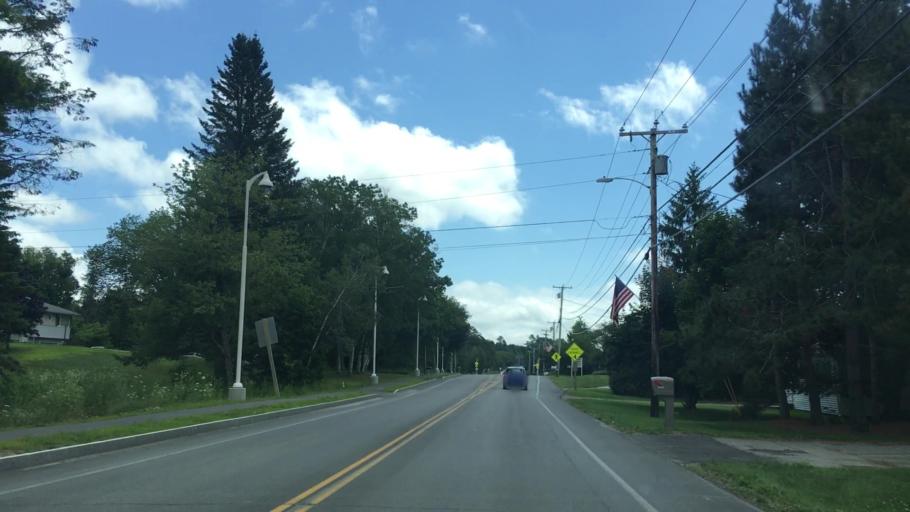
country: US
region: Maine
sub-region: Penobscot County
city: Hermon
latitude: 44.8072
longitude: -68.9053
